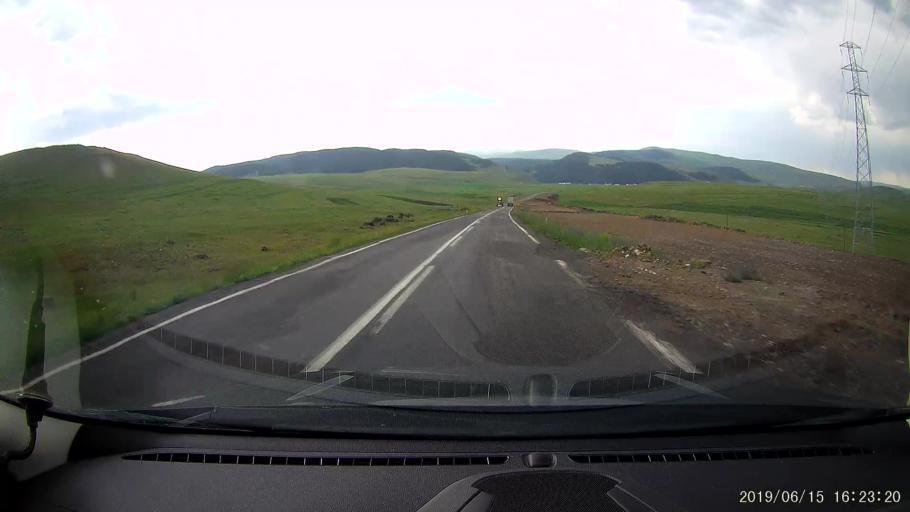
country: TR
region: Ardahan
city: Hanak
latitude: 41.1791
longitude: 42.8611
